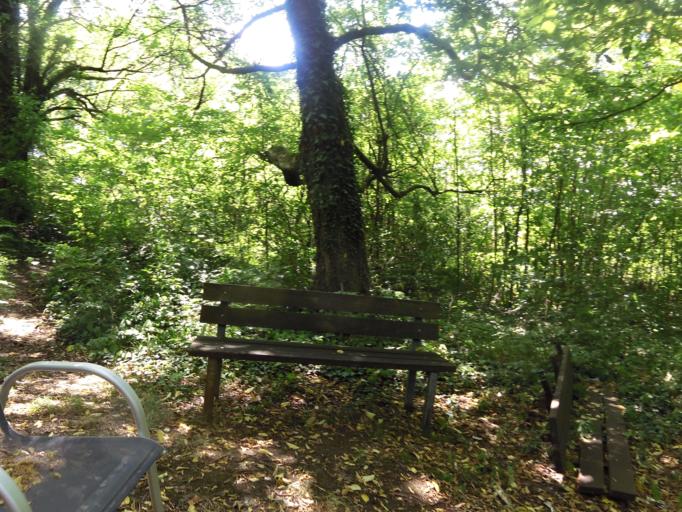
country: DE
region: Bavaria
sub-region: Regierungsbezirk Unterfranken
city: Randersacker
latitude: 49.7398
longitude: 9.9535
